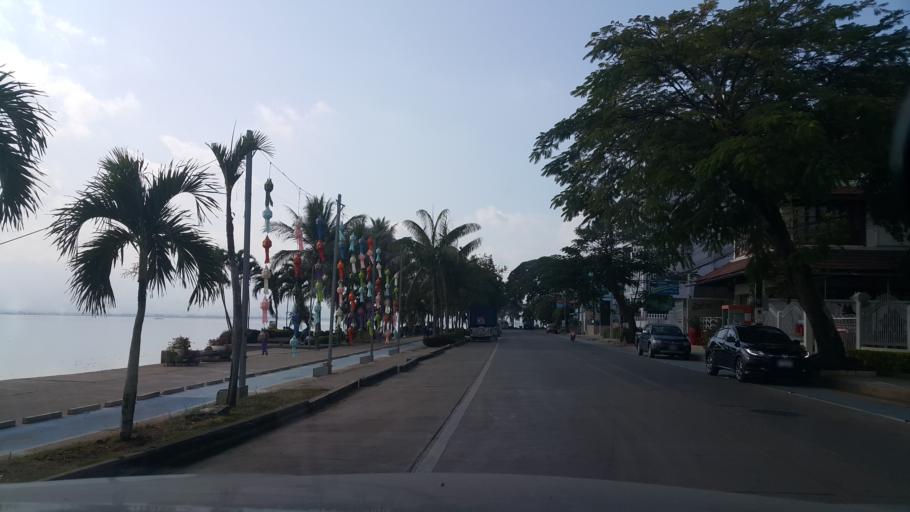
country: TH
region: Phayao
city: Phayao
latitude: 19.1637
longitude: 99.8991
